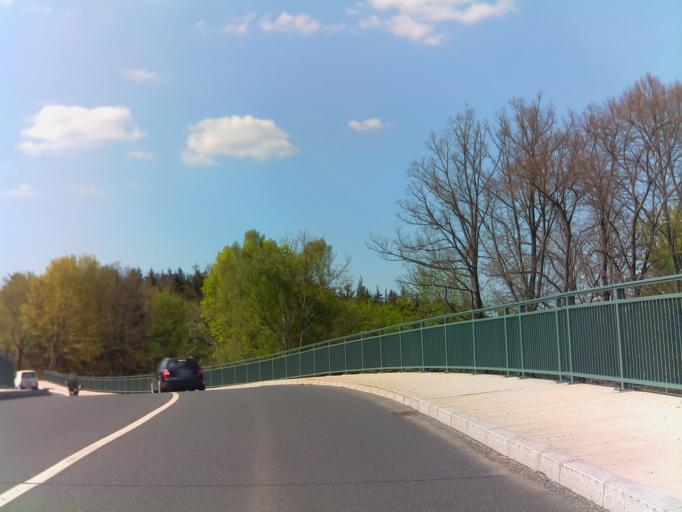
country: DE
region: Saxony
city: Mehltheuer
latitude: 50.5452
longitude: 12.0416
